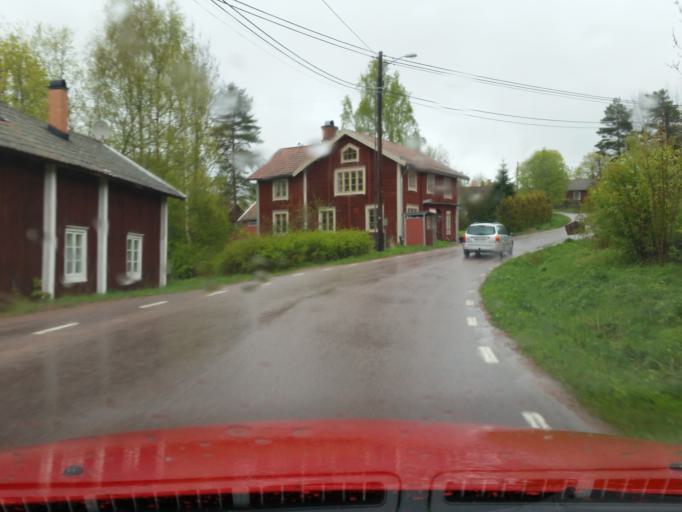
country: SE
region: Dalarna
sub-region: Saters Kommun
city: Saeter
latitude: 60.3579
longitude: 15.7843
